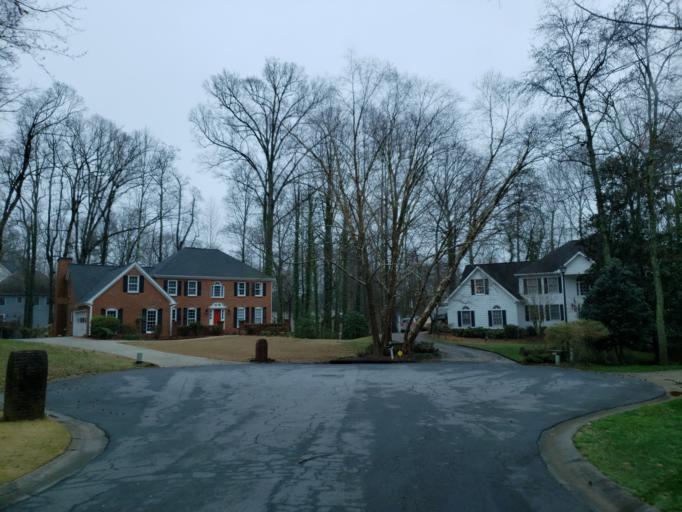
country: US
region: Georgia
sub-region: Cobb County
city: Fair Oaks
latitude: 33.9298
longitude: -84.5724
